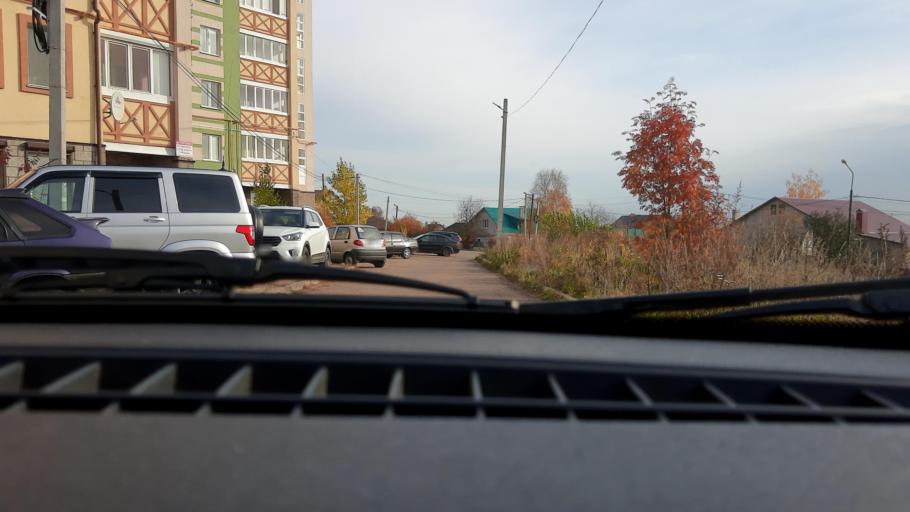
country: RU
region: Bashkortostan
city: Mikhaylovka
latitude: 54.8117
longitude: 55.8964
